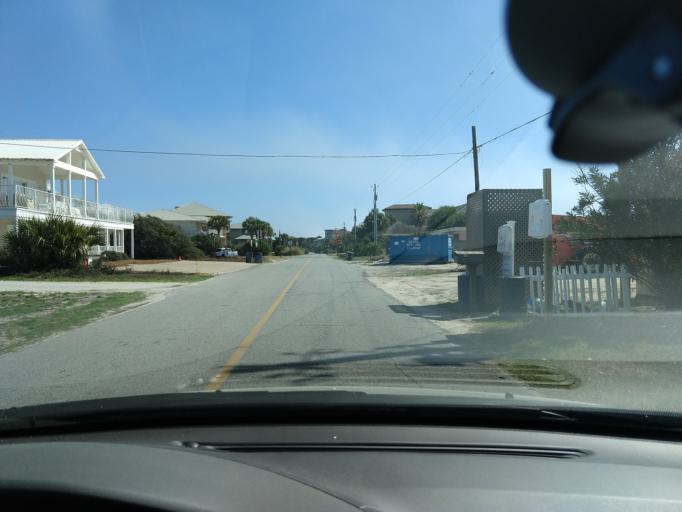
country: US
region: Florida
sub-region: Walton County
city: Seaside
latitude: 30.3372
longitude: -86.1973
